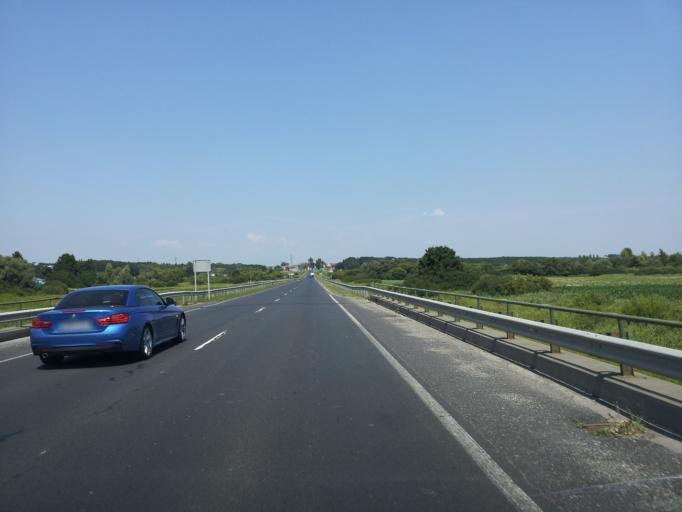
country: HU
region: Zala
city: Zalaegerszeg
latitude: 46.8525
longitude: 16.8611
